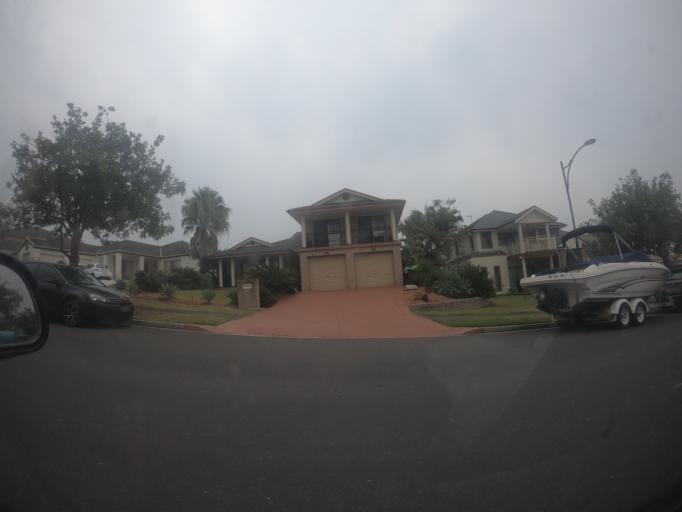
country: AU
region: New South Wales
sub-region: Shellharbour
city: Flinders
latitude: -34.5920
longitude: 150.8572
